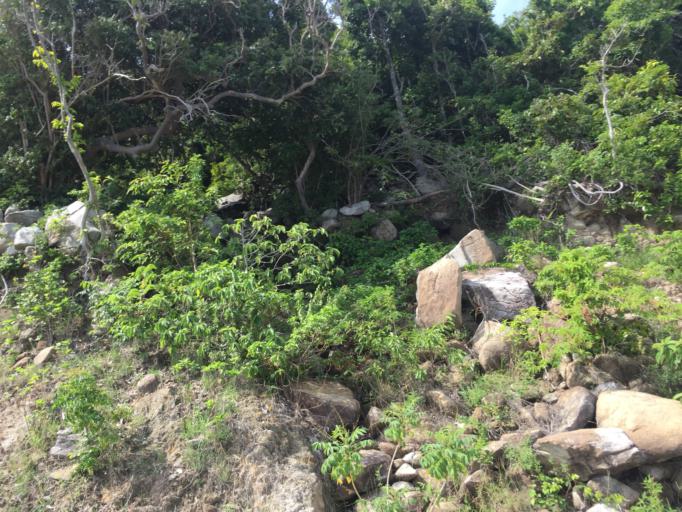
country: VN
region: Quang Nam
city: Hoi An
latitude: 15.9626
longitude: 108.5139
